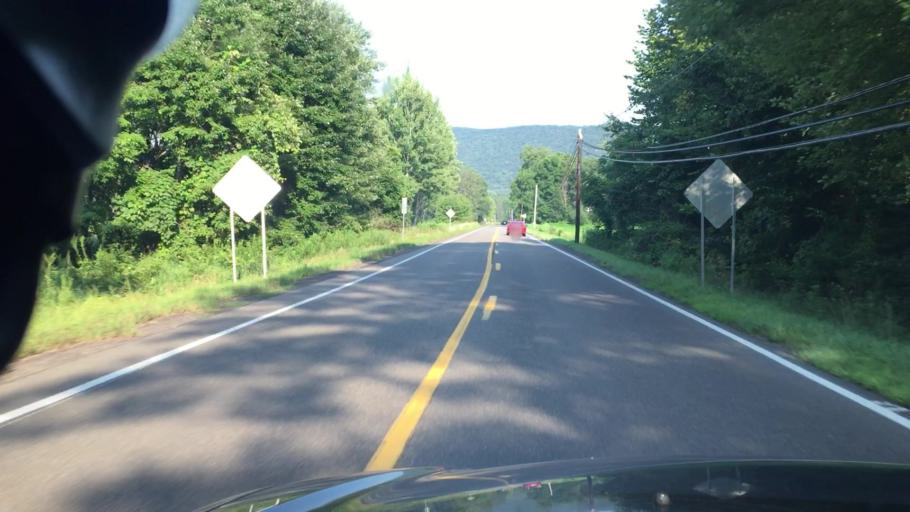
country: US
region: Pennsylvania
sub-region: Columbia County
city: Almedia
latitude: 40.9811
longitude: -76.3864
